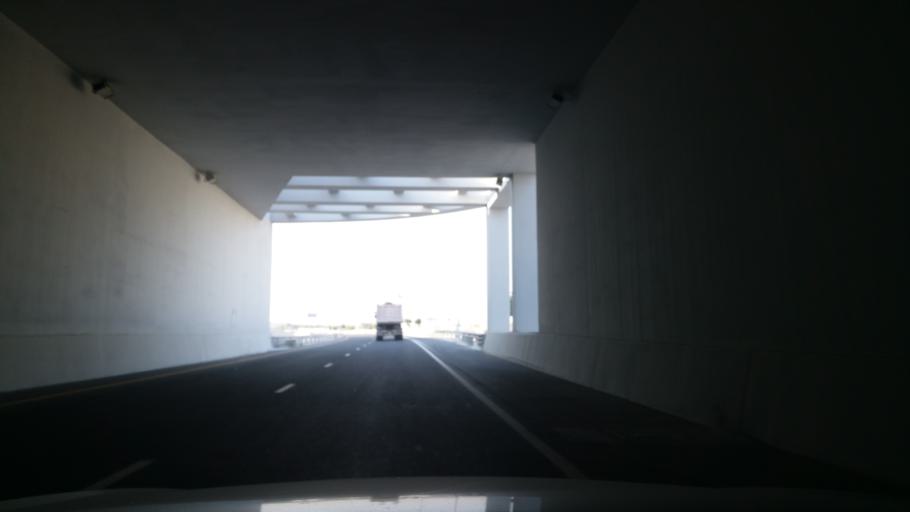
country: QA
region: Al Wakrah
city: Al Wakrah
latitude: 25.1562
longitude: 51.5724
